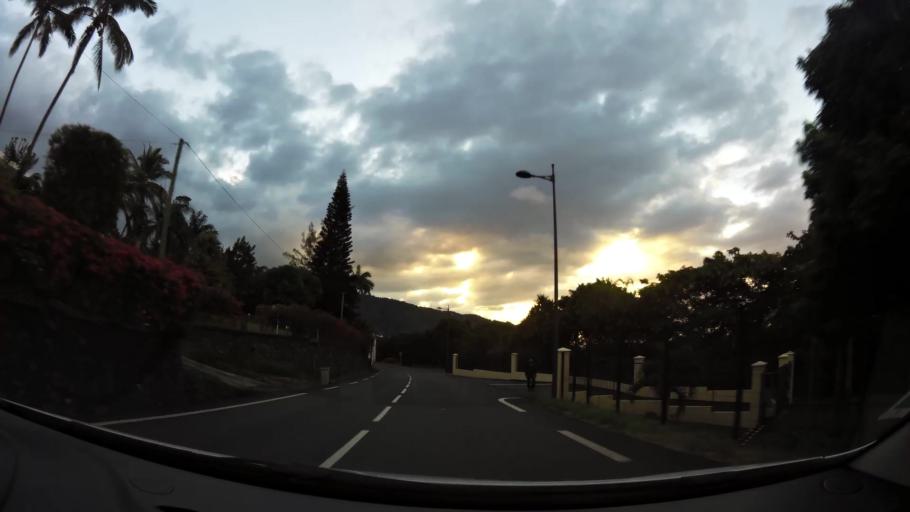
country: RE
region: Reunion
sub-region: Reunion
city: Saint-Denis
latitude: -20.9025
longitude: 55.4624
